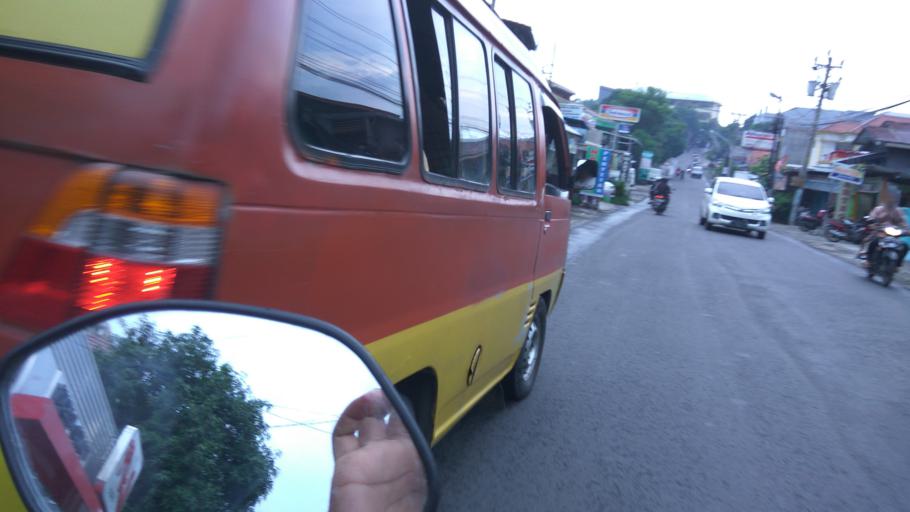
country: ID
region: Central Java
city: Semarang
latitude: -7.0294
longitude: 110.4092
